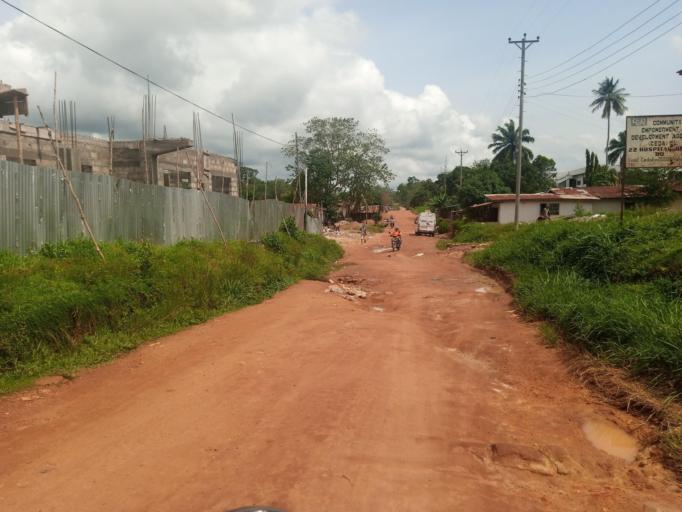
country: SL
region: Southern Province
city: Bo
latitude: 7.9660
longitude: -11.7431
